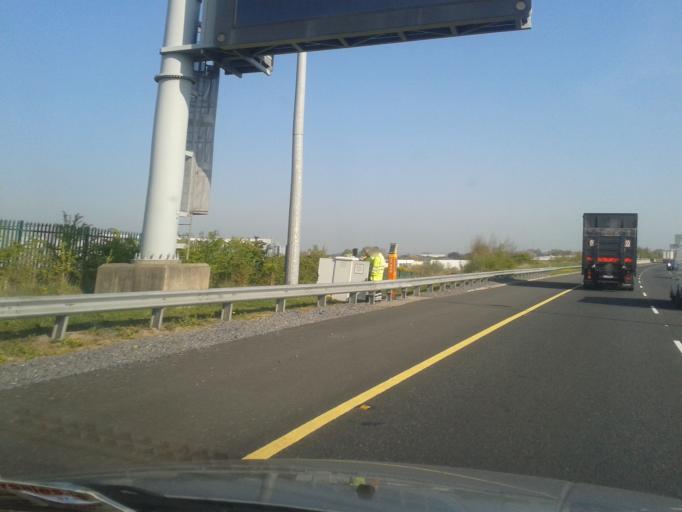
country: IE
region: Leinster
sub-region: Fingal County
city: Swords
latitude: 53.4593
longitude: -6.2041
